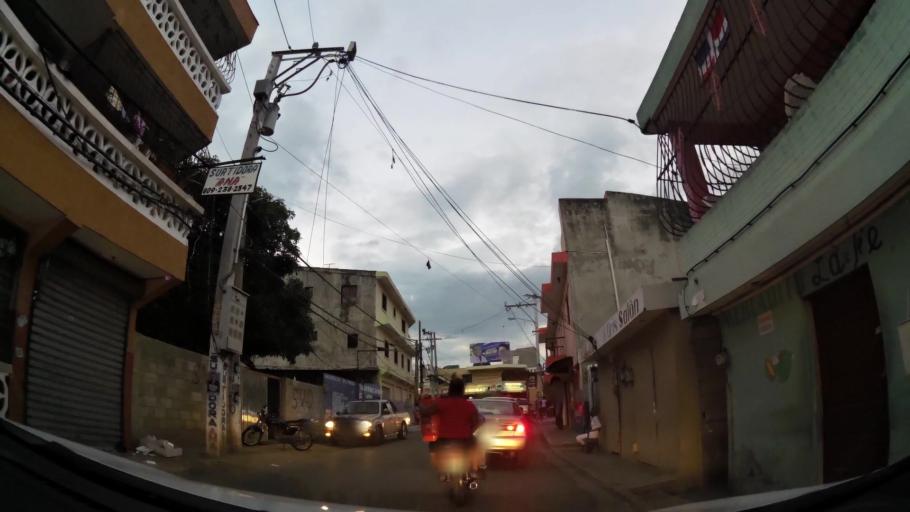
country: DO
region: Santo Domingo
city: Santo Domingo Oeste
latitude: 18.5232
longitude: -70.0328
